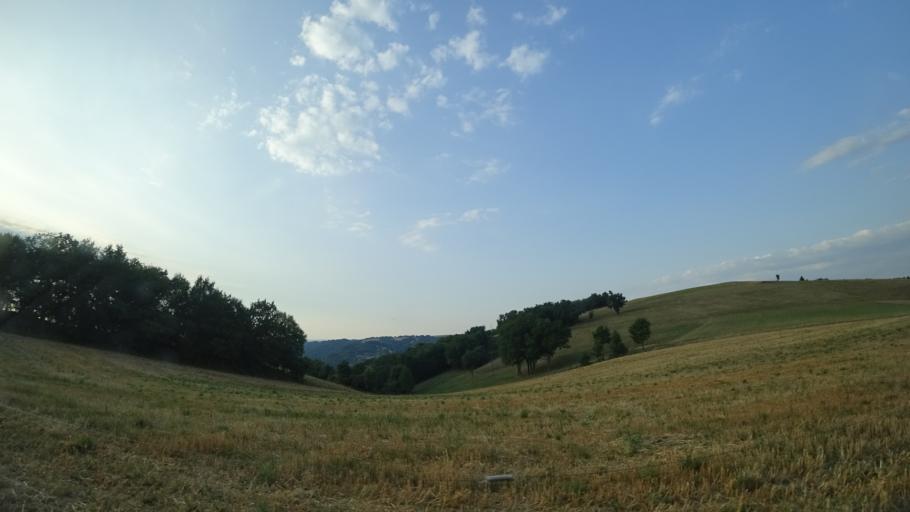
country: FR
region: Midi-Pyrenees
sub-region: Departement de l'Aveyron
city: Livinhac-le-Haut
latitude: 44.6009
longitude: 2.2546
